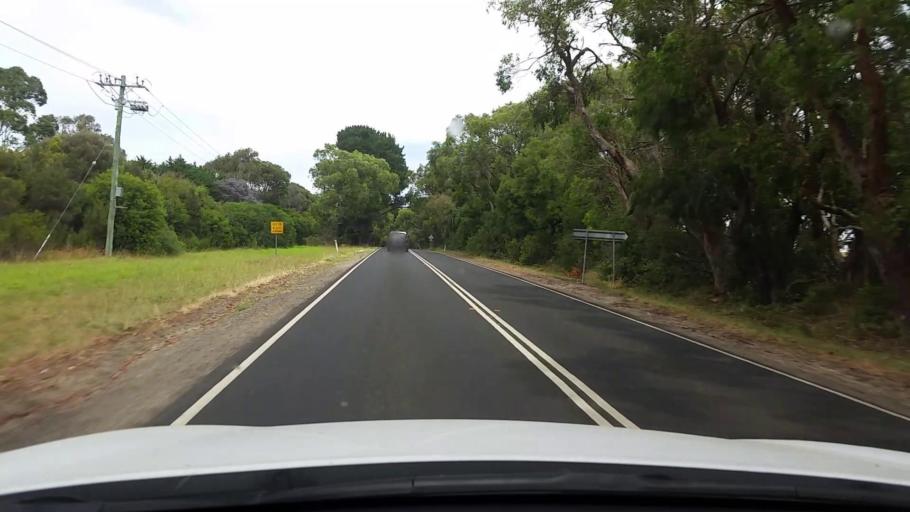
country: AU
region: Victoria
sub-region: Mornington Peninsula
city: Merricks
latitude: -38.4076
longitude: 145.0640
